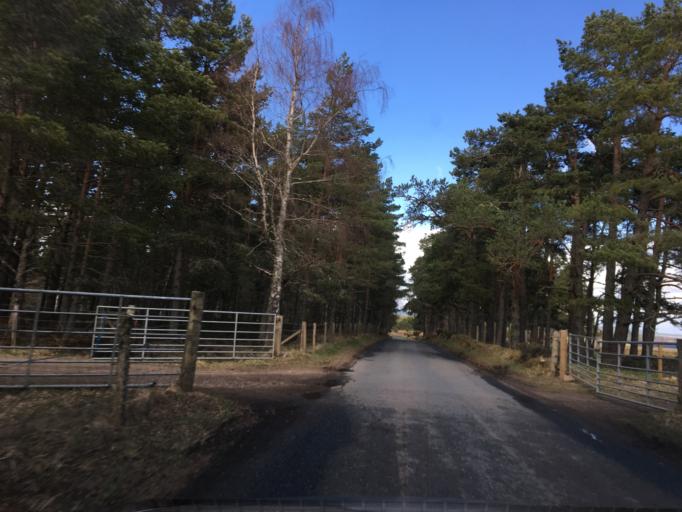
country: GB
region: Scotland
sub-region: Highland
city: Aviemore
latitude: 57.1829
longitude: -3.8003
